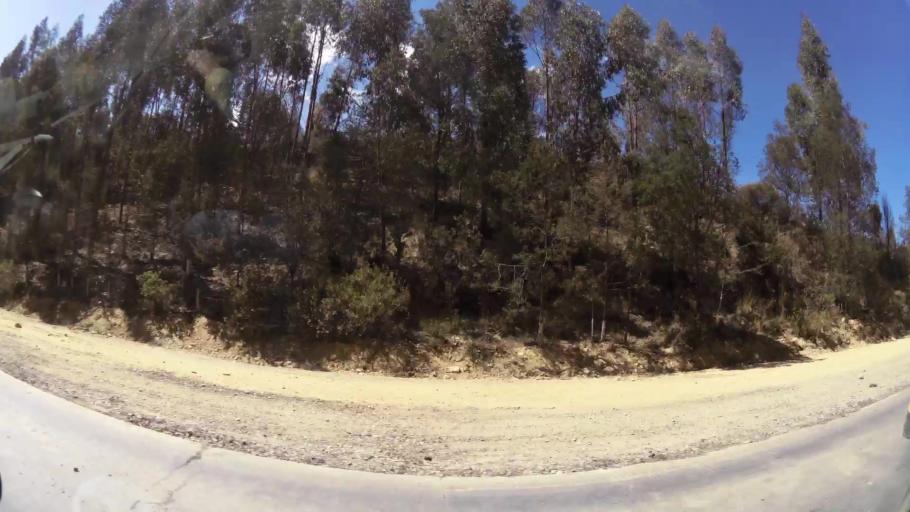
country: BO
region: La Paz
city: La Paz
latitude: -16.4799
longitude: -68.1600
